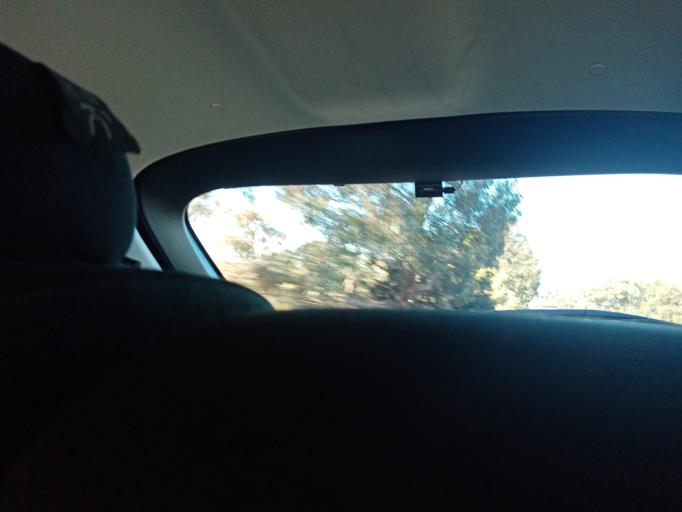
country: AU
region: Western Australia
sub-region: City of Cockburn
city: Yangebup
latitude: -32.1271
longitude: 115.8287
